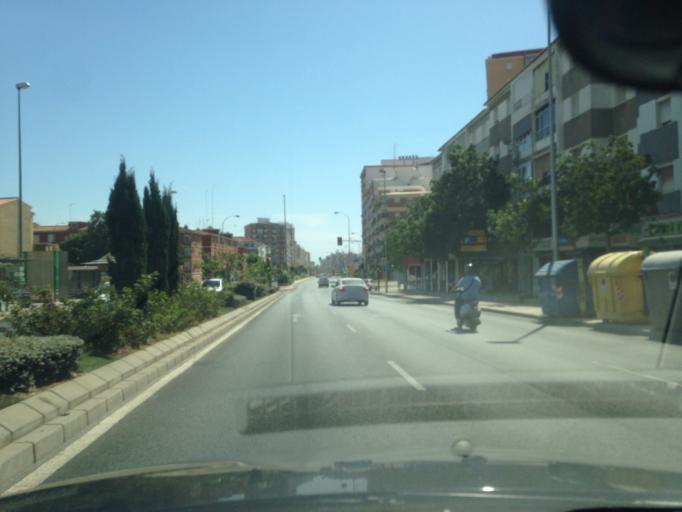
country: ES
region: Andalusia
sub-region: Provincia de Malaga
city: Malaga
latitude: 36.7121
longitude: -4.4465
